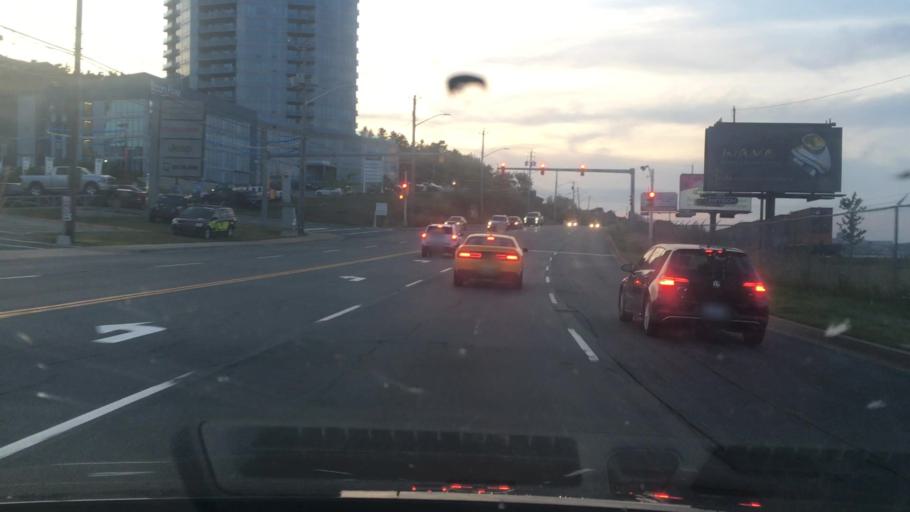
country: CA
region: Nova Scotia
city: Dartmouth
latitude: 44.6639
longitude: -63.6336
